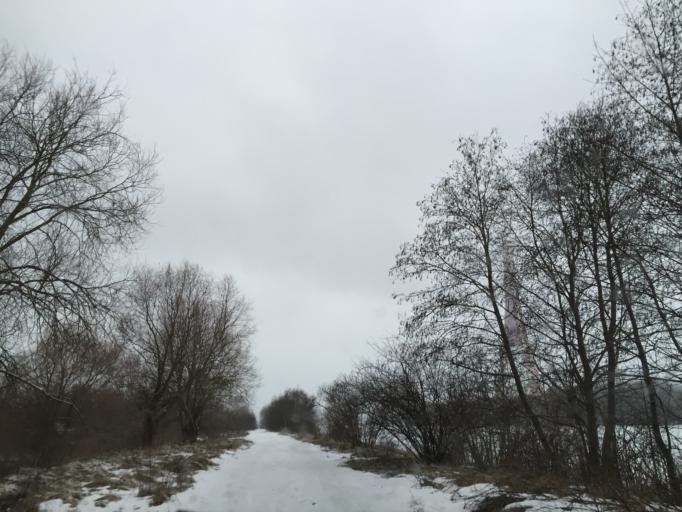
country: LV
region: Riga
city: Riga
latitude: 56.9180
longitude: 24.1418
